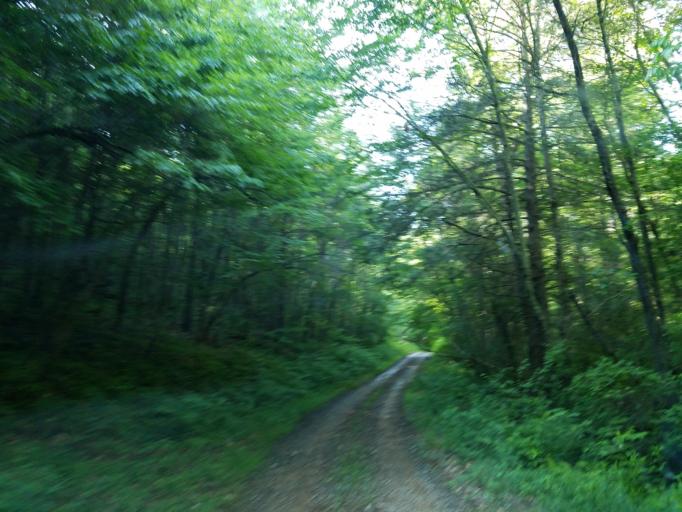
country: US
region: Georgia
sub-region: Fannin County
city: Blue Ridge
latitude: 34.7951
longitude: -84.2010
